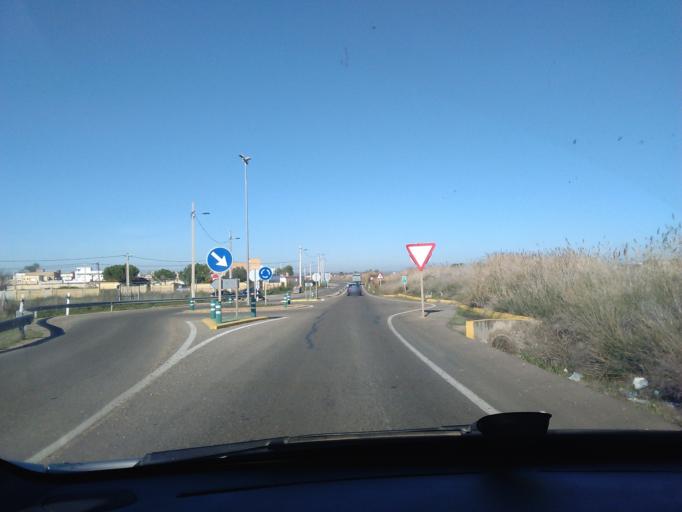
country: ES
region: Andalusia
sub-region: Provincia de Sevilla
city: La Rinconada
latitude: 37.4442
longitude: -5.9369
